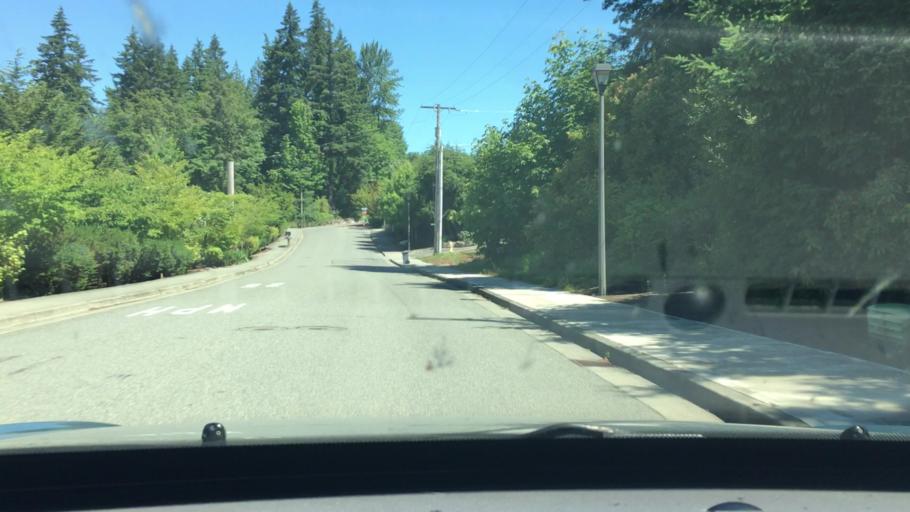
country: US
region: Washington
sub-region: King County
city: Newcastle
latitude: 47.5410
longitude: -122.1200
